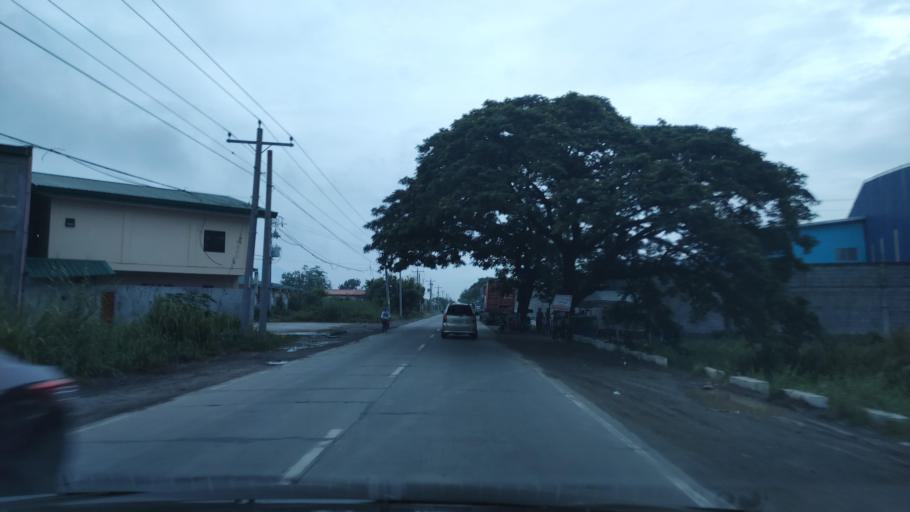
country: PH
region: Central Luzon
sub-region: Province of Pampanga
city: Laug
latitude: 15.0575
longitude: 120.7537
